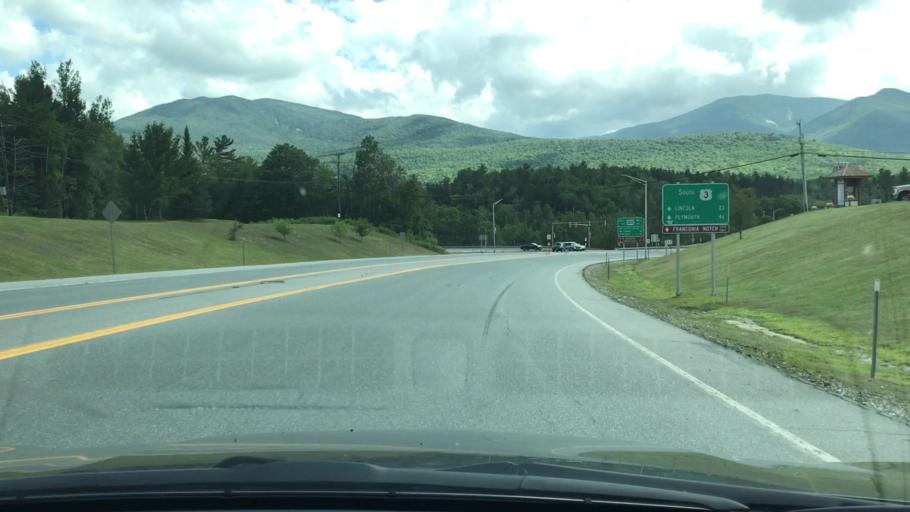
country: US
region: New Hampshire
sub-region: Grafton County
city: Deerfield
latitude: 44.2727
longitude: -71.5397
